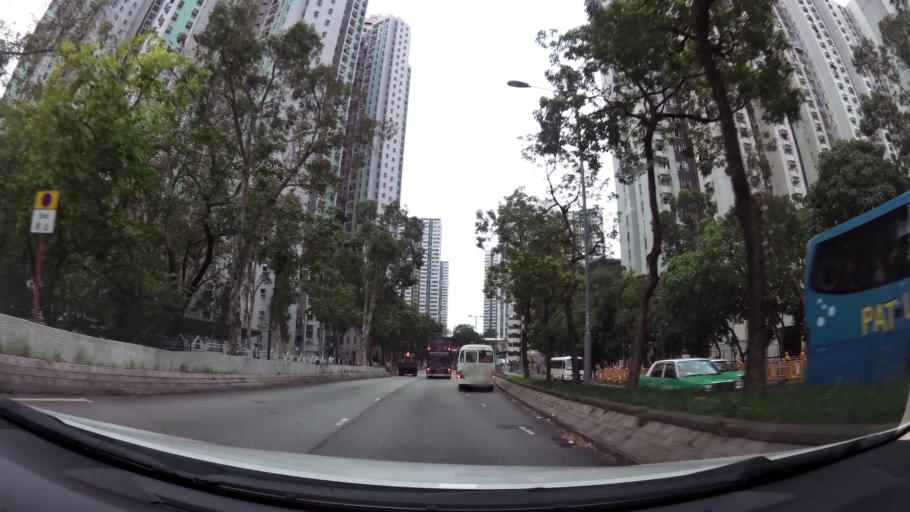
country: HK
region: Tai Po
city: Tai Po
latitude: 22.4547
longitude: 114.1727
